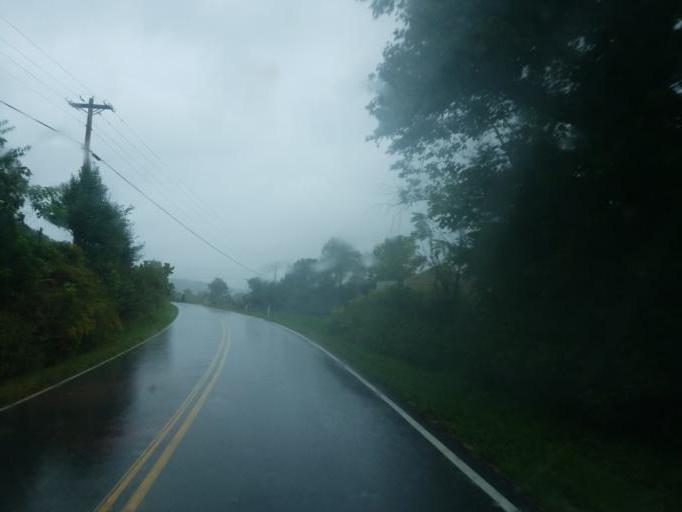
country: US
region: Kentucky
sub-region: Carter County
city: Grayson
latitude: 38.4739
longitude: -83.0347
